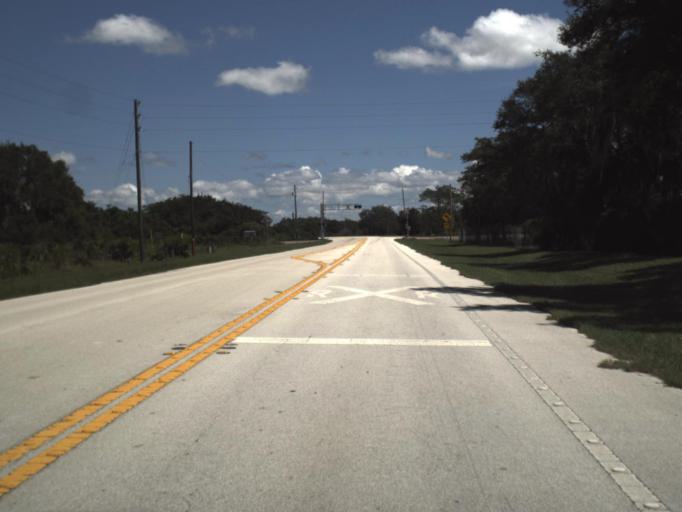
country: US
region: Florida
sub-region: Polk County
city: Frostproof
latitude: 27.6801
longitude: -81.5511
